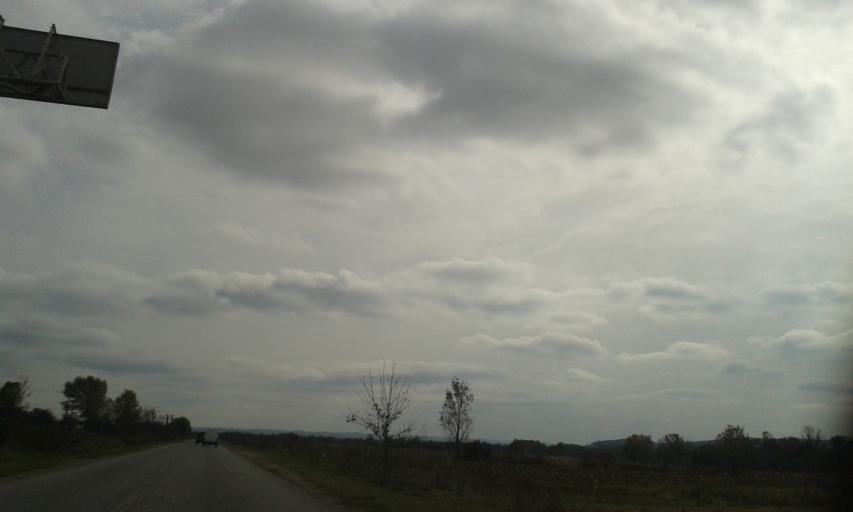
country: RO
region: Gorj
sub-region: Comuna Scoarta
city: Scoarta
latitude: 45.0157
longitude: 23.4688
